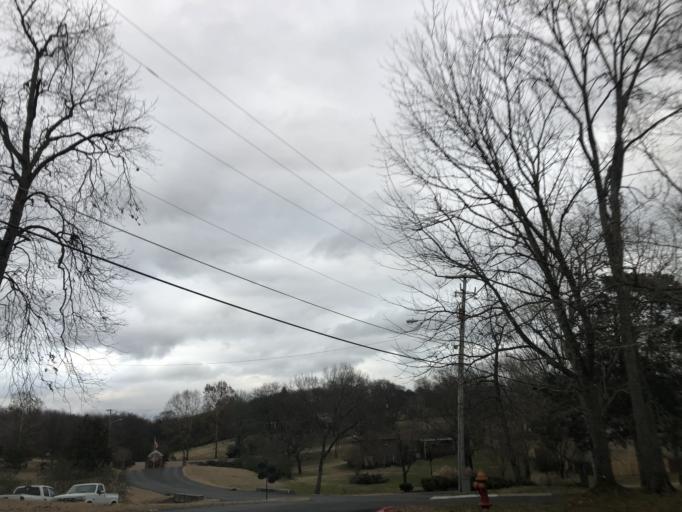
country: US
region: Tennessee
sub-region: Davidson County
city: Goodlettsville
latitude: 36.2961
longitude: -86.6885
